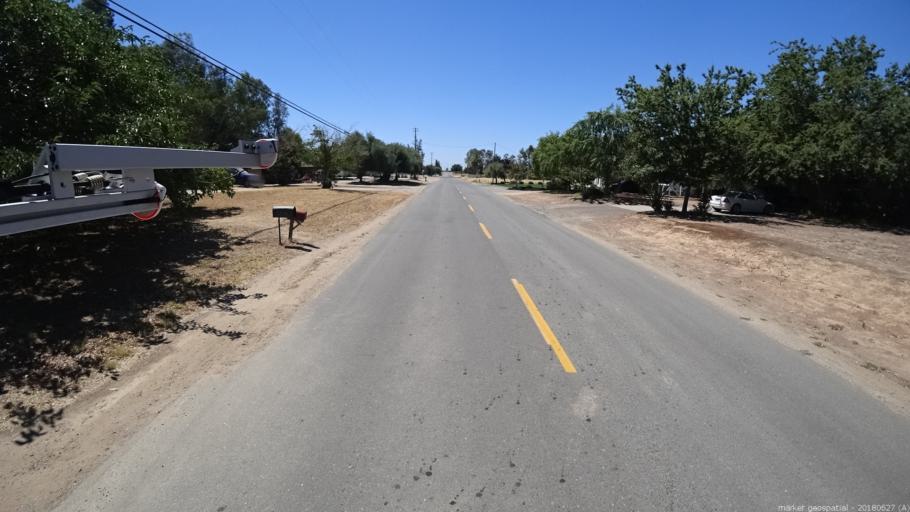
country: US
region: California
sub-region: Madera County
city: Bonadelle Ranchos-Madera Ranchos
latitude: 36.9347
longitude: -119.9032
